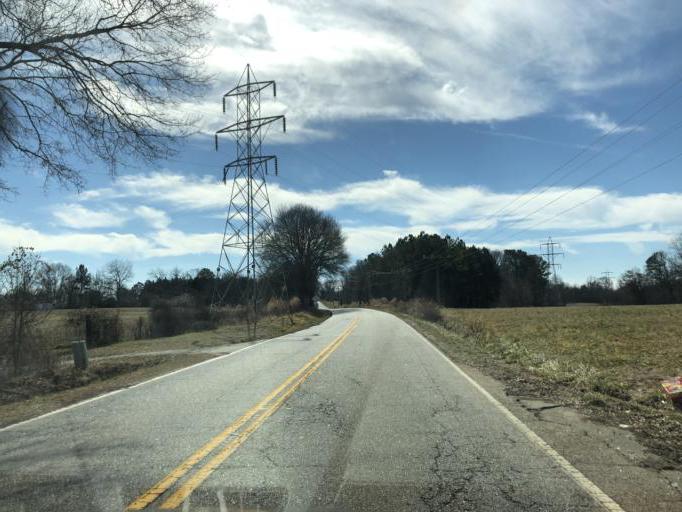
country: US
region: South Carolina
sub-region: Spartanburg County
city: Mayo
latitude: 35.0416
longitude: -81.8800
